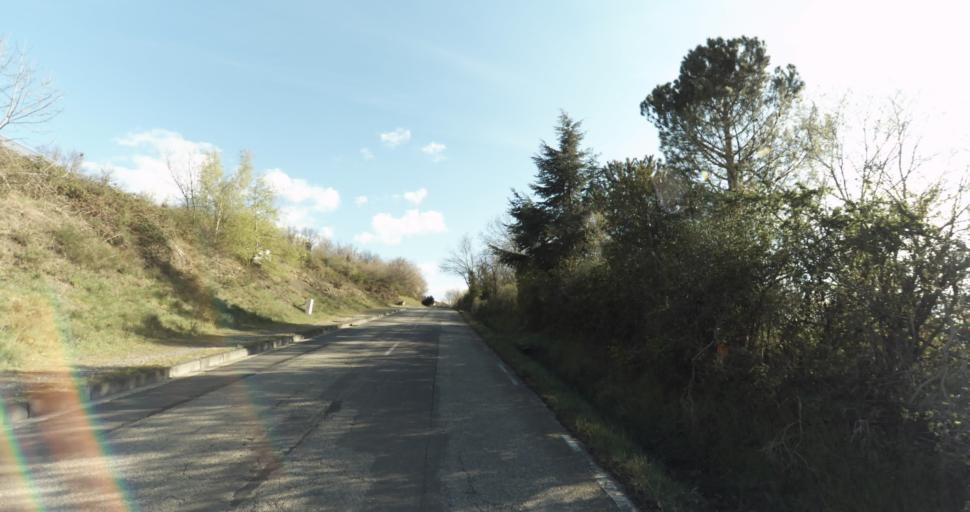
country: FR
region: Rhone-Alpes
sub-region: Departement de la Loire
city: Saint-Jean-Bonnefonds
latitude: 45.4558
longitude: 4.4261
